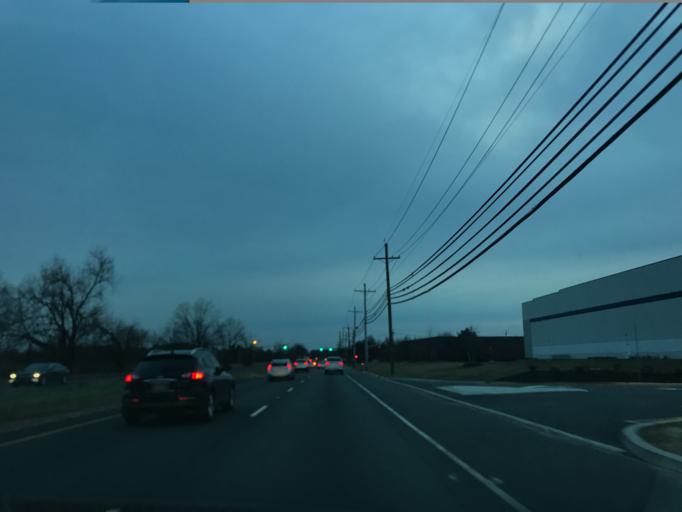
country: US
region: New Jersey
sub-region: Middlesex County
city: Cranbury
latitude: 40.3398
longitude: -74.5015
